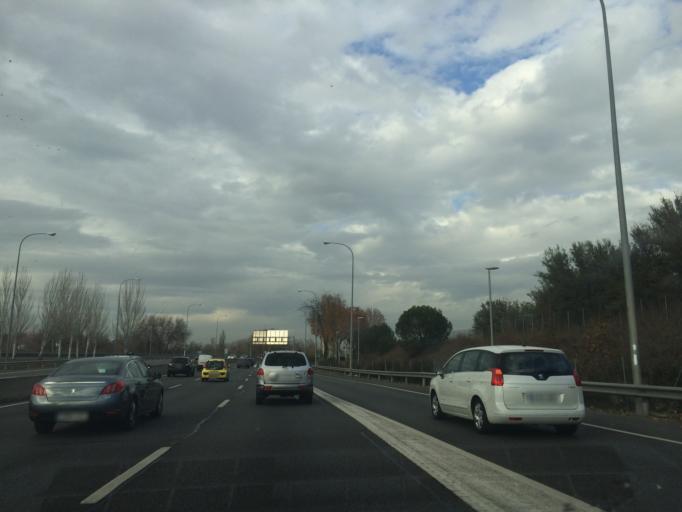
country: ES
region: Madrid
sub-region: Provincia de Madrid
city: Moncloa-Aravaca
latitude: 40.4387
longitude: -3.7380
